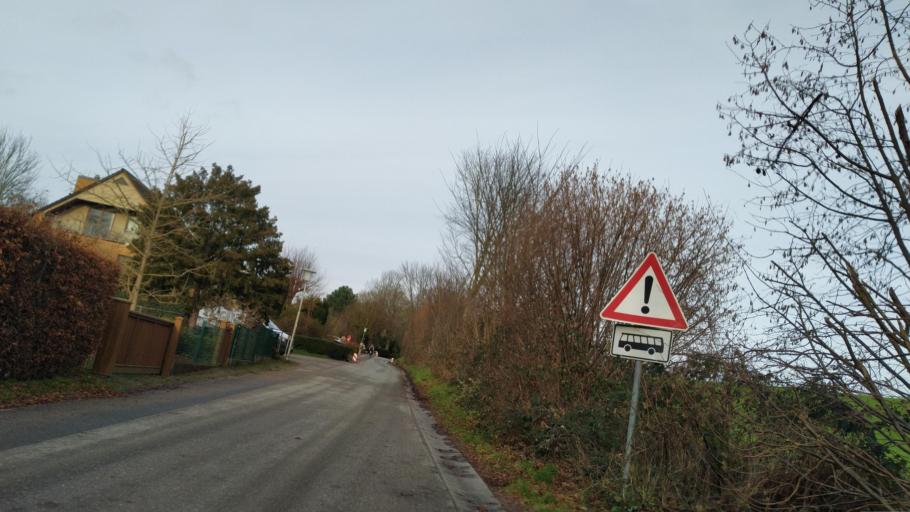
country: DE
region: Schleswig-Holstein
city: Eutin
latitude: 54.1891
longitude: 10.6069
